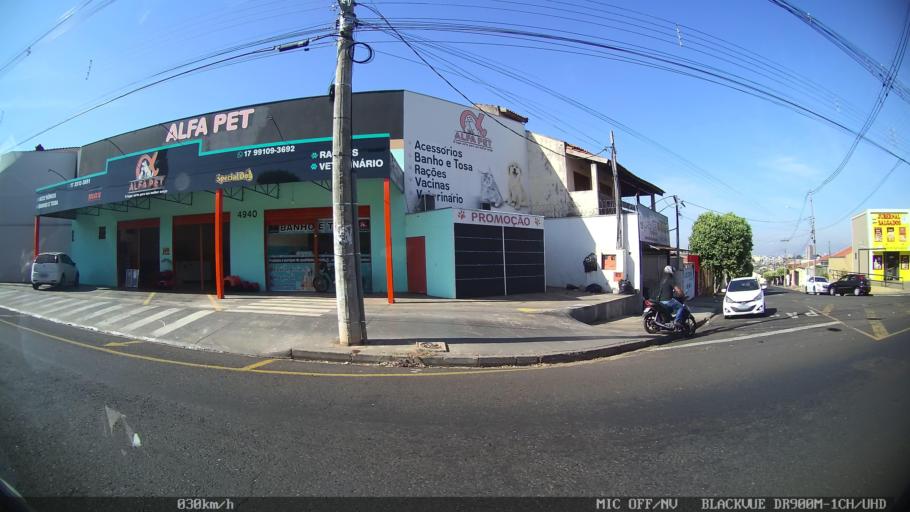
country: BR
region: Sao Paulo
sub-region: Sao Jose Do Rio Preto
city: Sao Jose do Rio Preto
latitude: -20.7725
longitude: -49.3933
